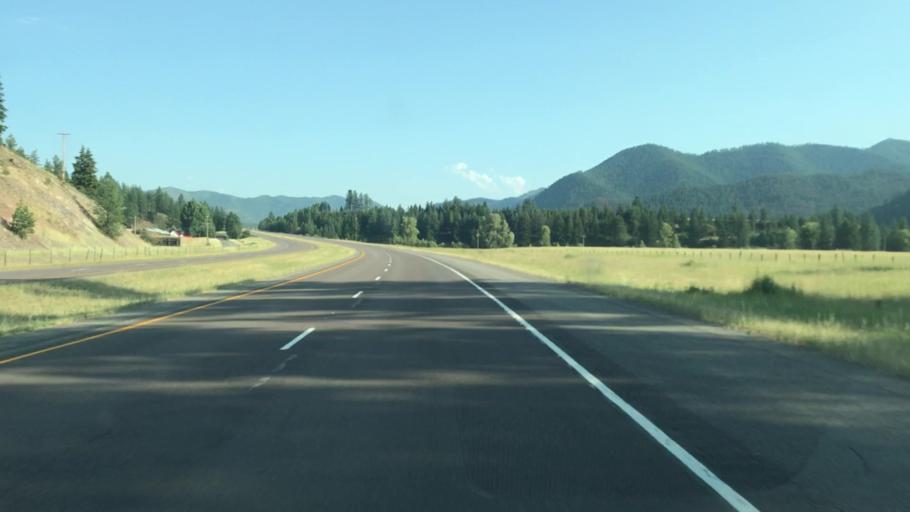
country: US
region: Montana
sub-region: Mineral County
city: Superior
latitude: 47.0586
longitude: -114.7627
